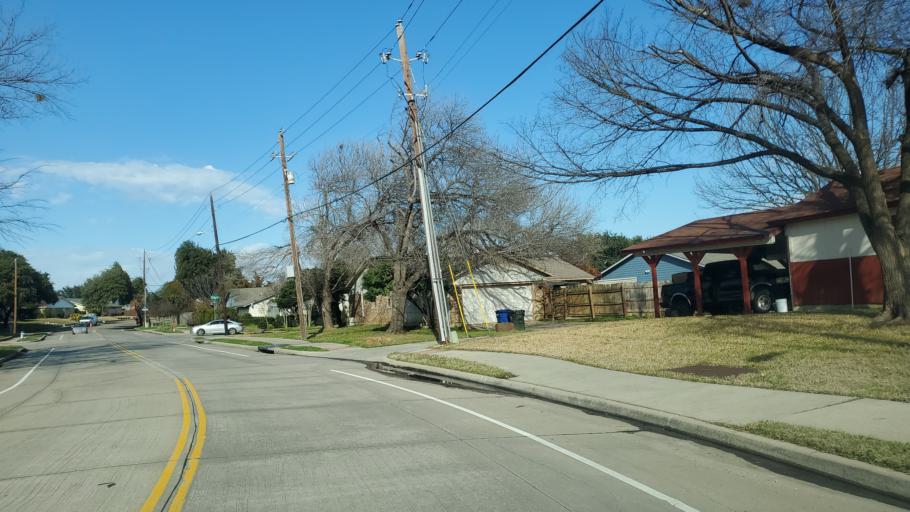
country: US
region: Texas
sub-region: Dallas County
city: Carrollton
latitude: 32.9912
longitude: -96.8830
